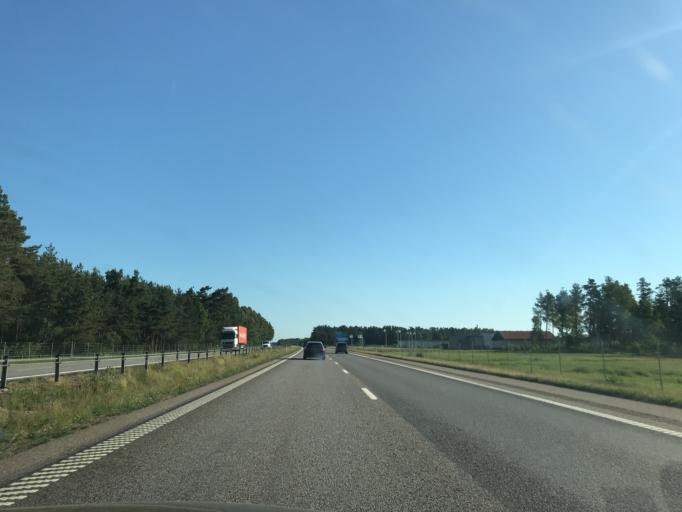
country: SE
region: Halland
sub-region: Laholms Kommun
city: Mellbystrand
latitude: 56.4920
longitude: 12.9543
